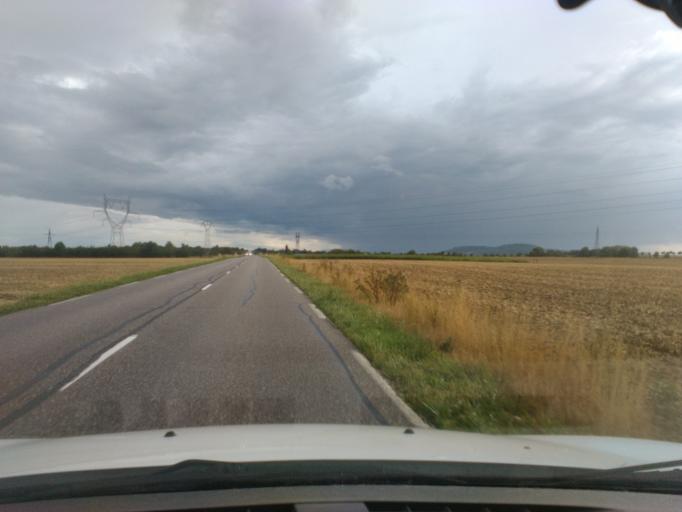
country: FR
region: Lorraine
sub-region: Departement de Meurthe-et-Moselle
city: Vezelise
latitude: 48.4824
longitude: 6.1425
